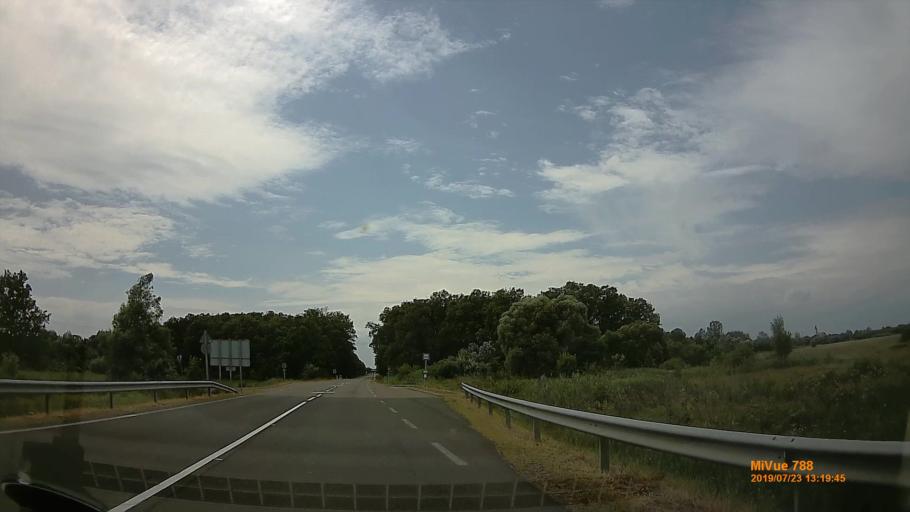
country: HU
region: Hajdu-Bihar
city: Polgar
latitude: 47.8718
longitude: 21.1360
